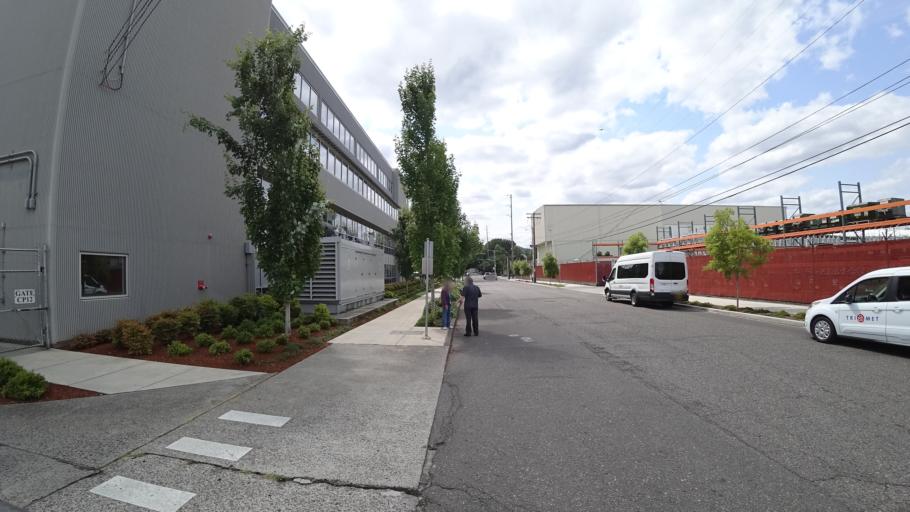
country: US
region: Oregon
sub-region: Multnomah County
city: Portland
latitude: 45.4939
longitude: -122.6468
